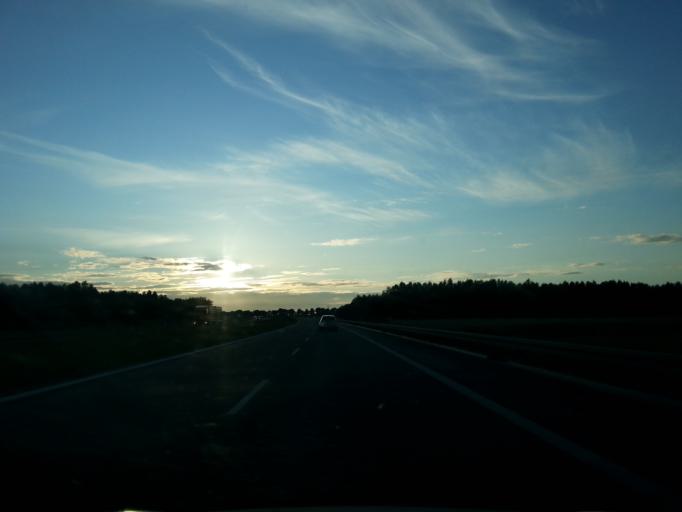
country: PL
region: Lodz Voivodeship
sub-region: Powiat wieruszowski
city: Wieruszow
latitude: 51.3317
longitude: 18.1454
